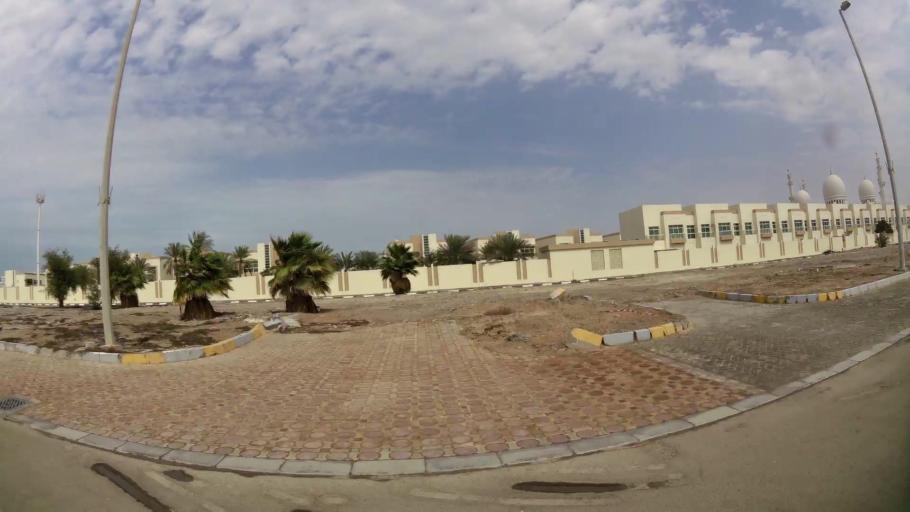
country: AE
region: Abu Dhabi
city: Abu Dhabi
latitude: 24.4108
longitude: 54.4690
